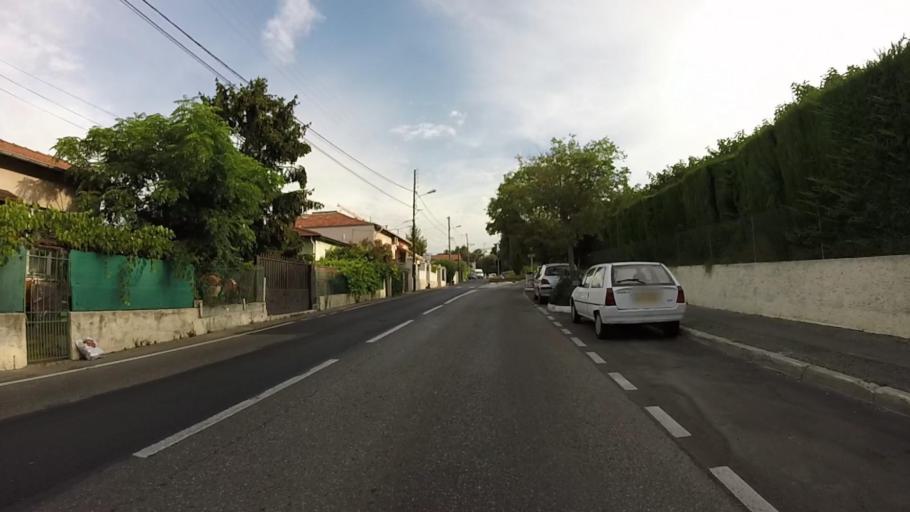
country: FR
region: Provence-Alpes-Cote d'Azur
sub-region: Departement des Alpes-Maritimes
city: Biot
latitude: 43.5945
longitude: 7.1067
